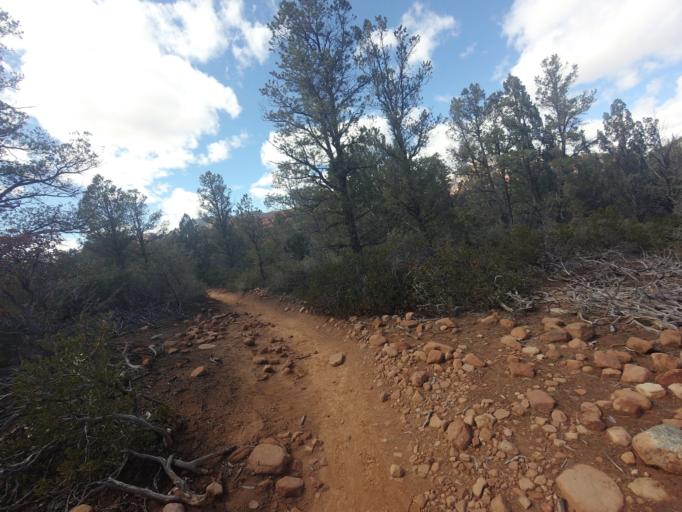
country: US
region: Arizona
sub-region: Yavapai County
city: West Sedona
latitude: 34.9001
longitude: -111.8239
